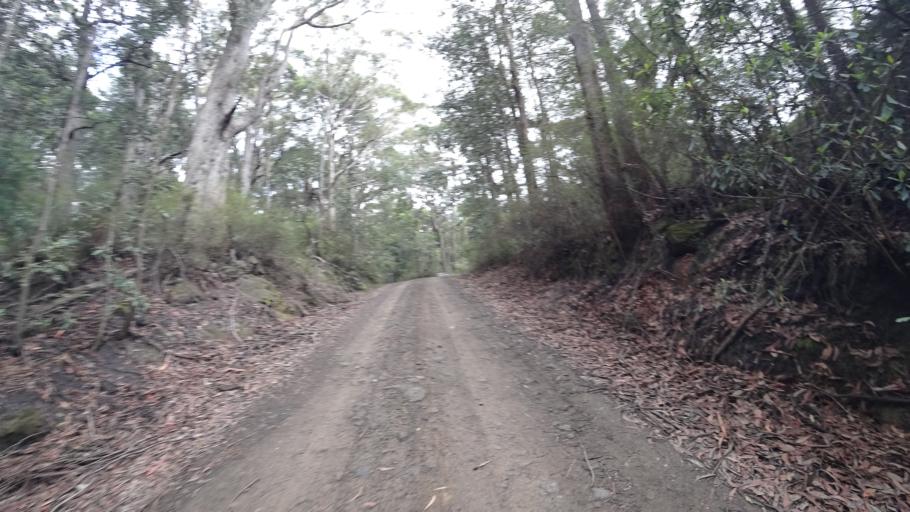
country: AU
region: New South Wales
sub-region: Shoalhaven Shire
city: Milton
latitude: -35.1734
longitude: 150.3725
